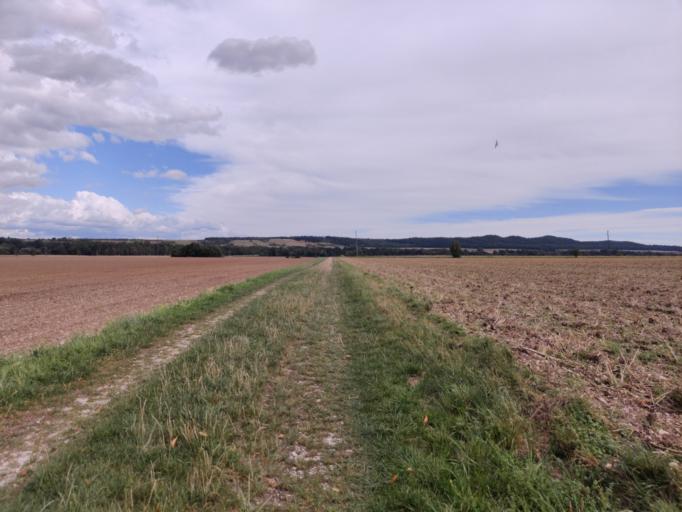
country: DE
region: Lower Saxony
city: Alt Wallmoden
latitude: 52.0153
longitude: 10.3352
